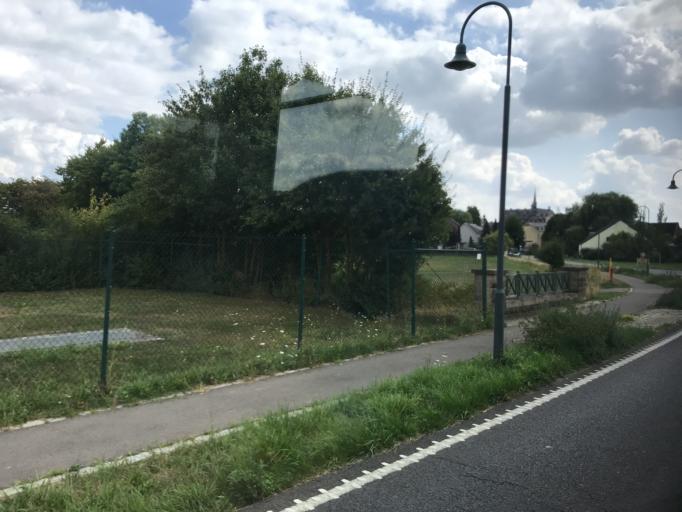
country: LU
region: Luxembourg
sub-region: Canton d'Esch-sur-Alzette
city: Bettembourg
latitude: 49.5250
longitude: 6.1238
